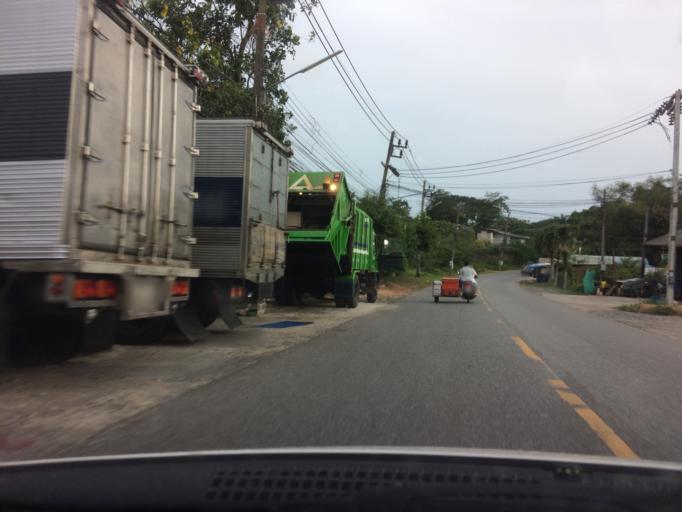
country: TH
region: Phuket
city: Phuket
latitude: 7.8918
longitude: 98.4071
